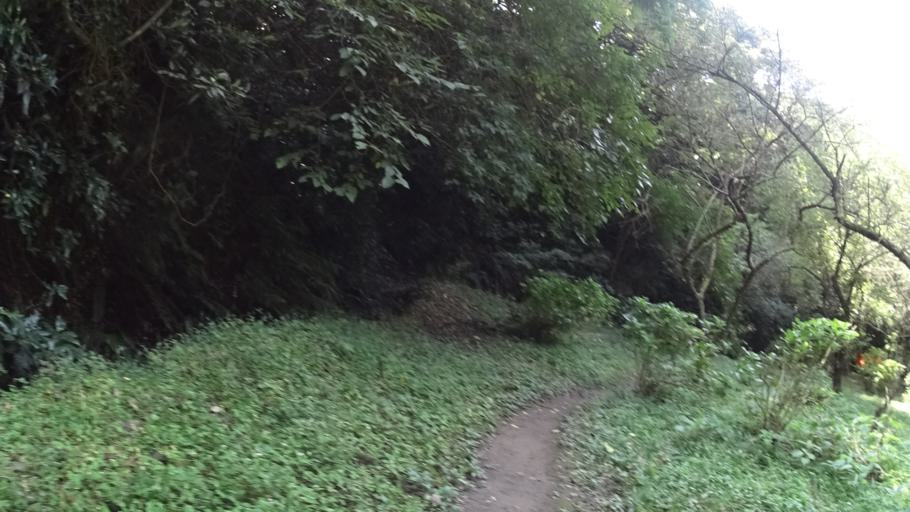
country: JP
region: Kanagawa
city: Kamakura
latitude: 35.3611
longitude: 139.5883
